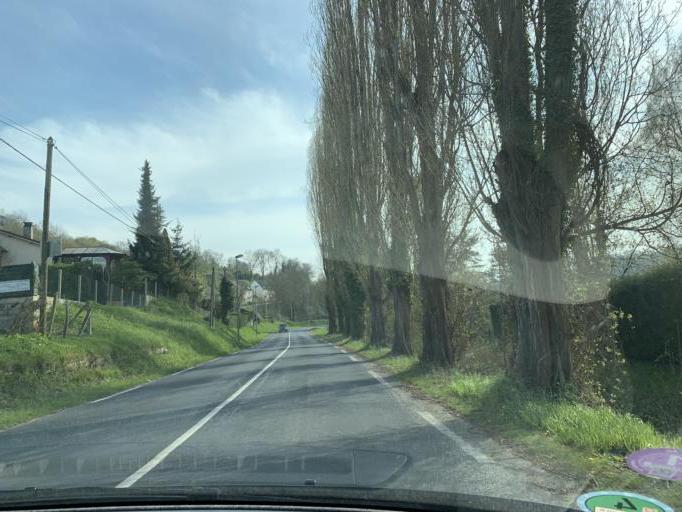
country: FR
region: Haute-Normandie
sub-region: Departement de l'Eure
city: Les Andelys
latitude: 49.2569
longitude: 1.4182
